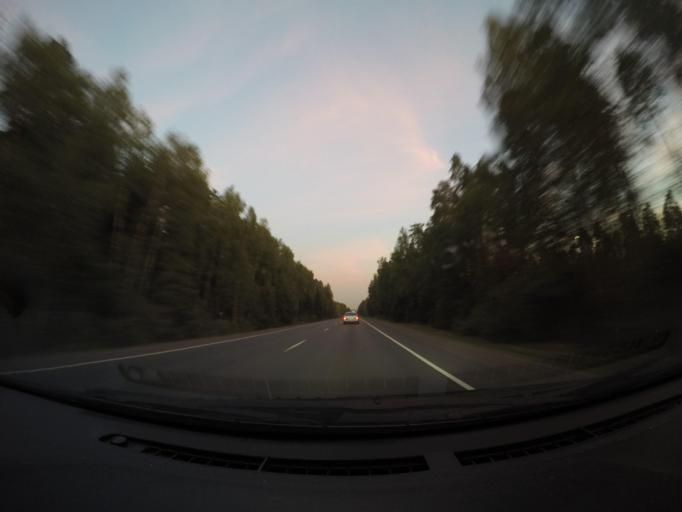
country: RU
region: Moskovskaya
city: Gzhel'
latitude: 55.5569
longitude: 38.3981
